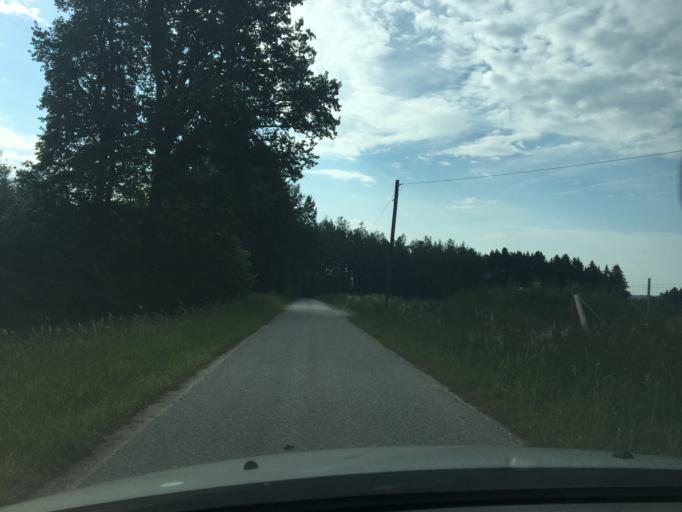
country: DE
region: Bavaria
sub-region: Upper Bavaria
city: Egglkofen
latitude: 48.4109
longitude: 12.4254
